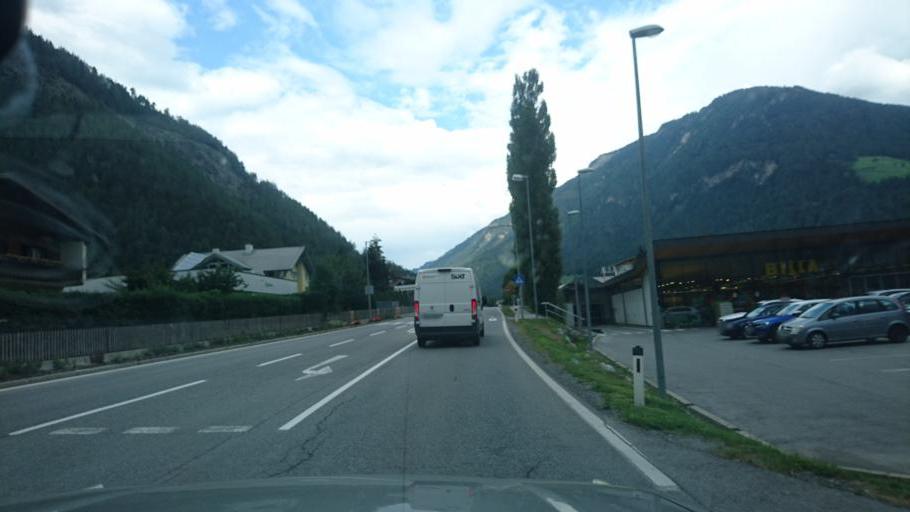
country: AT
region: Tyrol
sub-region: Politischer Bezirk Landeck
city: Pfunds
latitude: 46.9675
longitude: 10.5306
